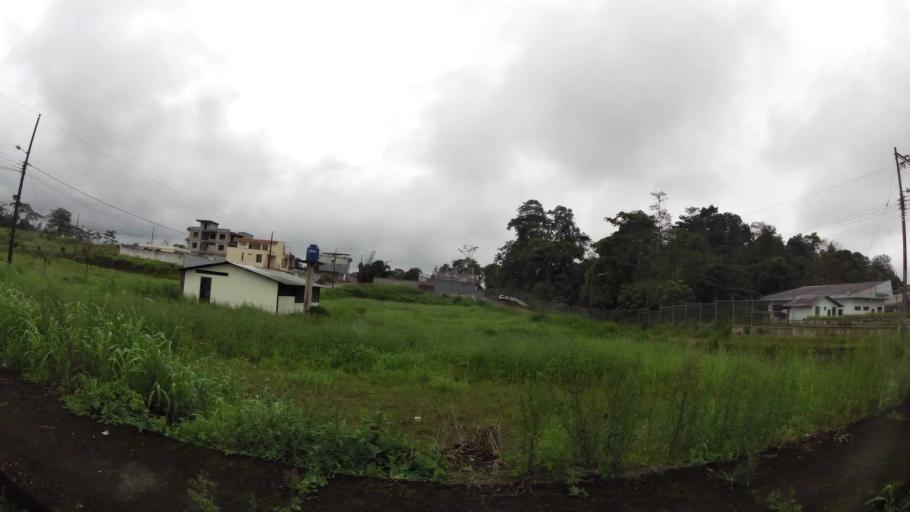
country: EC
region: Santo Domingo de los Tsachilas
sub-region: Canton Santo Domingo de los Colorados
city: Santo Domingo de los Colorados
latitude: -0.2515
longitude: -79.1438
